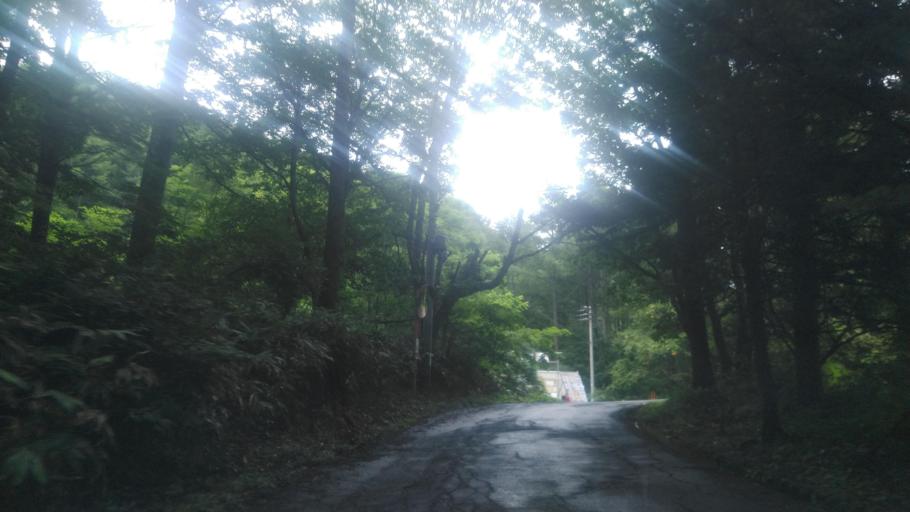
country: JP
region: Nagano
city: Ueda
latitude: 36.4969
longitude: 138.3887
